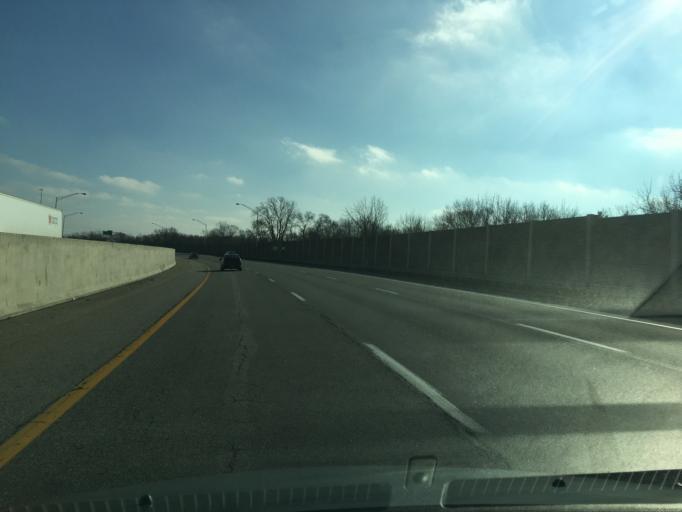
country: US
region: Indiana
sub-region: Marion County
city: Speedway
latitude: 39.8448
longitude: -86.2594
